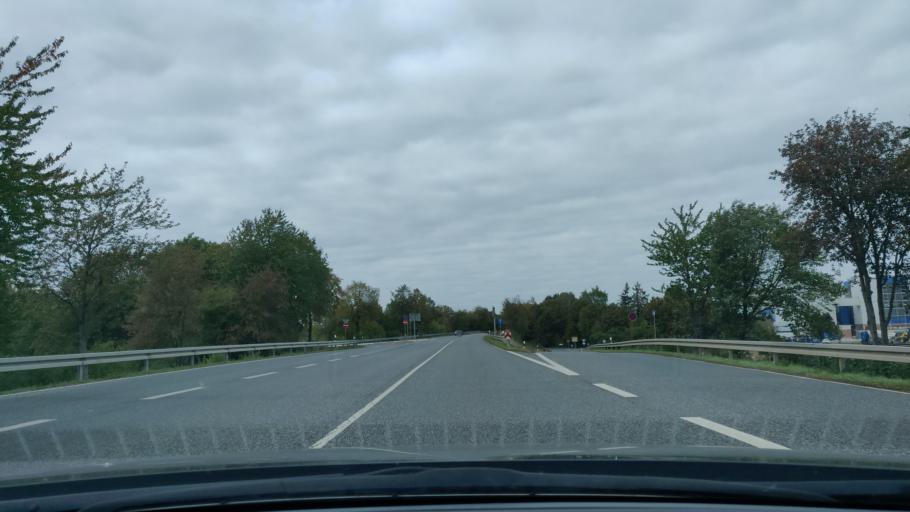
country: DE
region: Hesse
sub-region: Regierungsbezirk Kassel
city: Wabern
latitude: 51.0992
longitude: 9.3607
